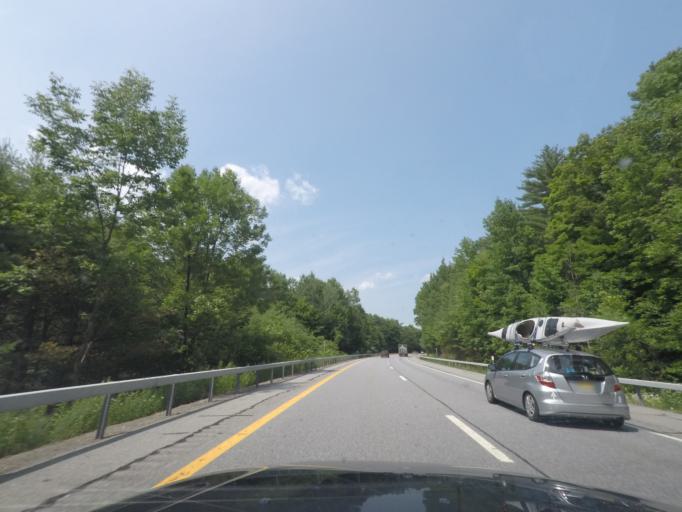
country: US
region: New York
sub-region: Warren County
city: Warrensburg
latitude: 43.5113
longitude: -73.7435
